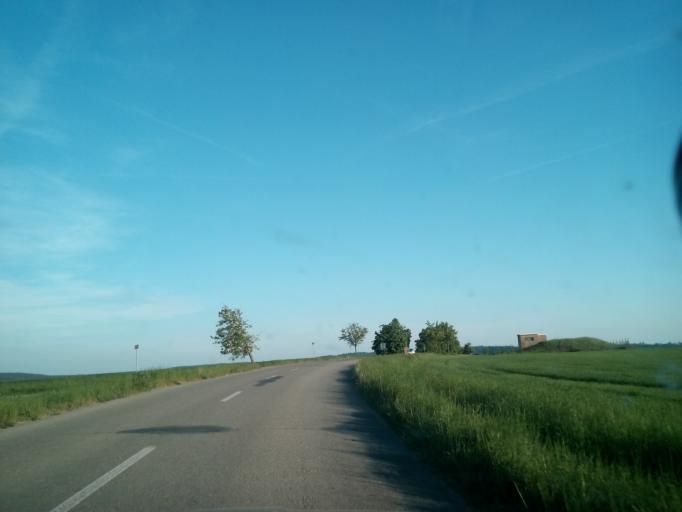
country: CZ
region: South Moravian
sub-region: Okres Blansko
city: Jedovnice
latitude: 49.3580
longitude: 16.7551
